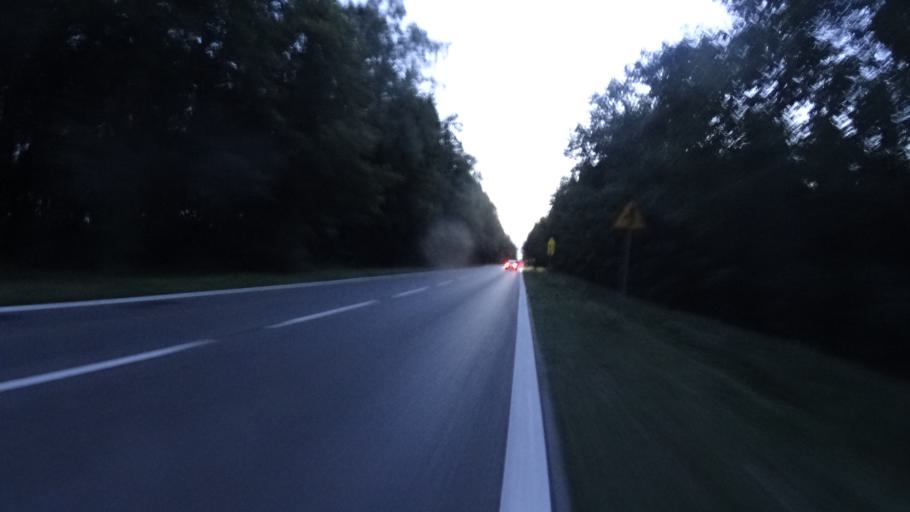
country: PL
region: Masovian Voivodeship
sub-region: Powiat warszawski zachodni
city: Leszno
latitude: 52.2632
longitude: 20.6561
